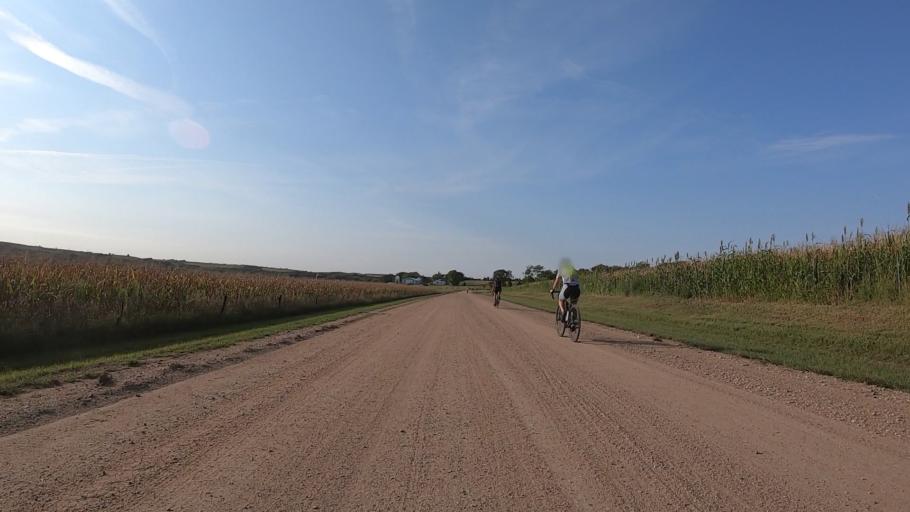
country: US
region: Kansas
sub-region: Marshall County
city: Blue Rapids
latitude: 39.6783
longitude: -96.7839
